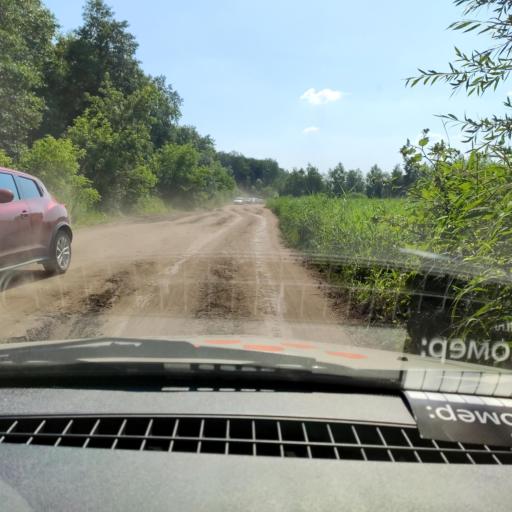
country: RU
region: Bashkortostan
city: Avdon
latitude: 54.6529
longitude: 55.8011
